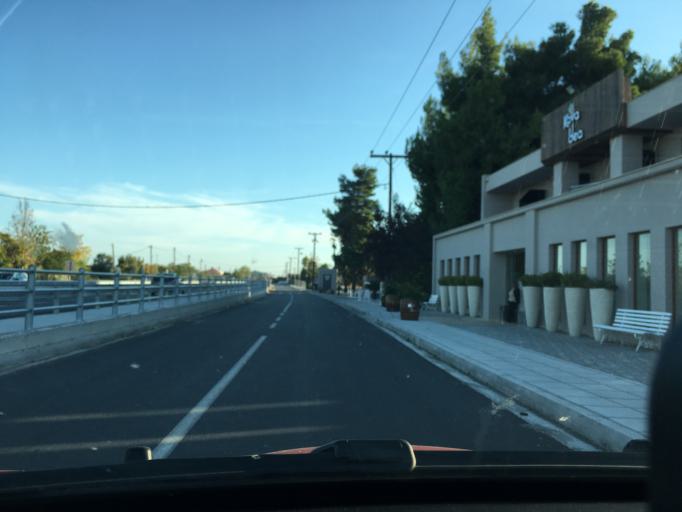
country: GR
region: Central Macedonia
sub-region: Nomos Chalkidikis
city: Nea Potidhaia
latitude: 40.2098
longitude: 23.3220
